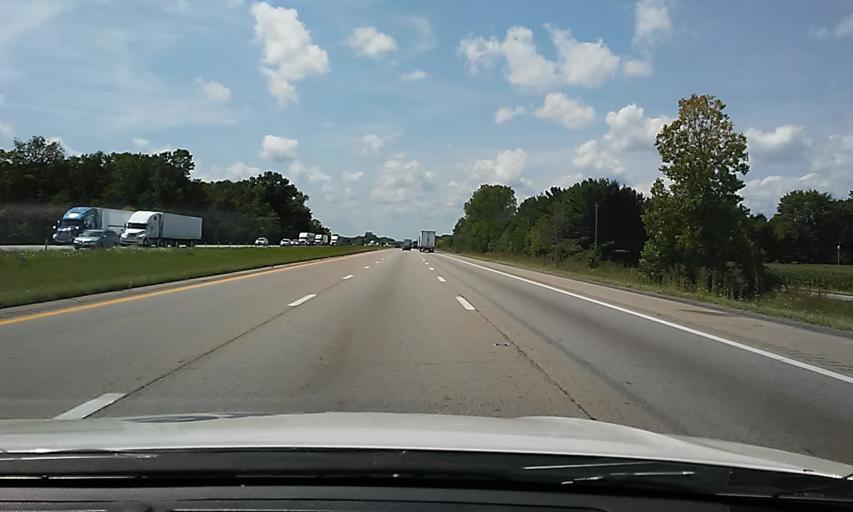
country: US
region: Ohio
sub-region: Franklin County
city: Lake Darby
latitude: 39.9800
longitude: -83.2069
